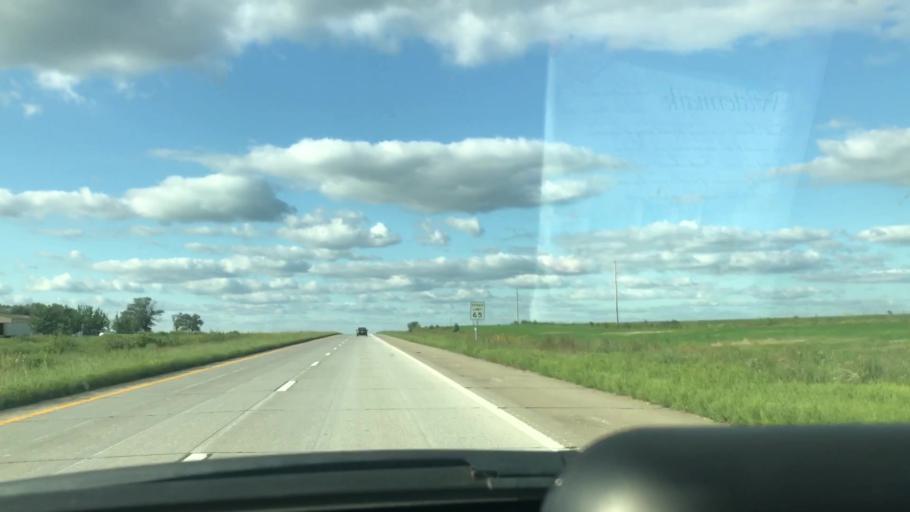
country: US
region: Missouri
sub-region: Benton County
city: Cole Camp
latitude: 38.4996
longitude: -93.2732
